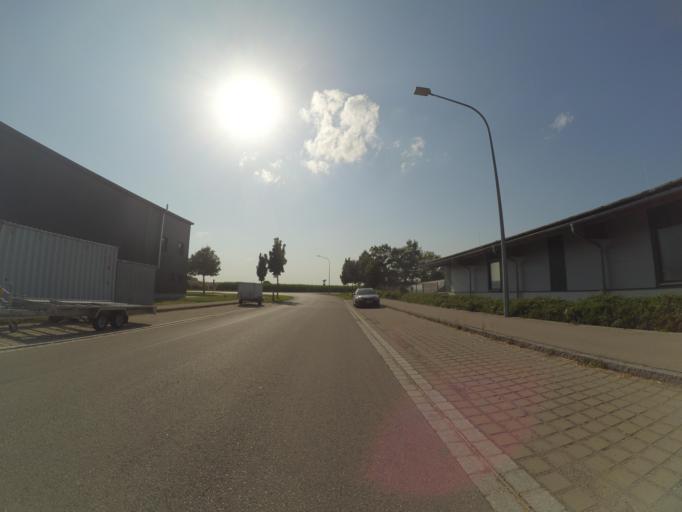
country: DE
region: Bavaria
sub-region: Swabia
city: Buchloe
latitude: 48.0440
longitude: 10.7028
